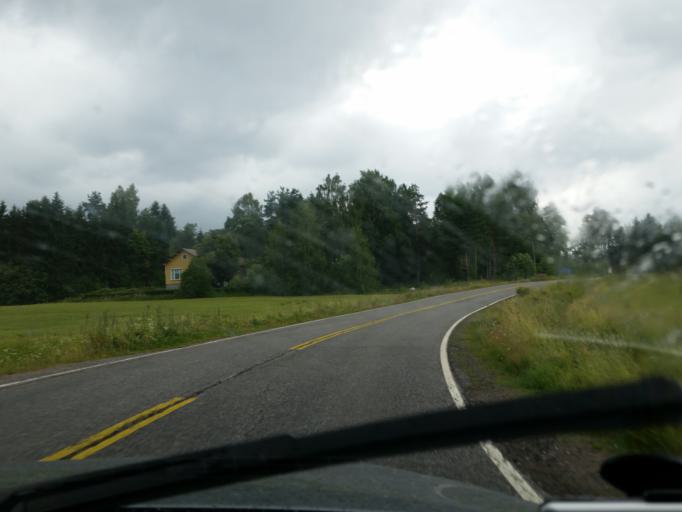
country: FI
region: Uusimaa
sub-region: Helsinki
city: Kaerkoelae
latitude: 60.5067
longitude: 23.9638
